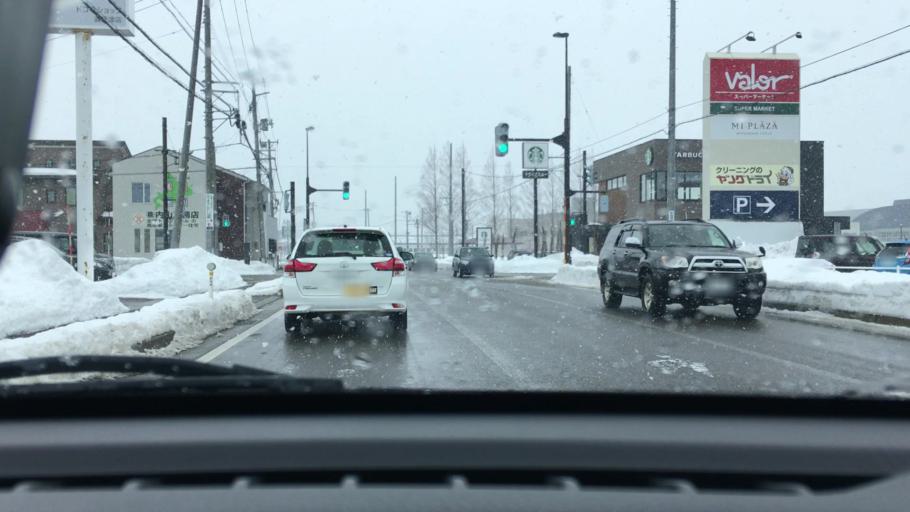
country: JP
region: Niigata
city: Joetsu
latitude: 37.1585
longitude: 138.2535
